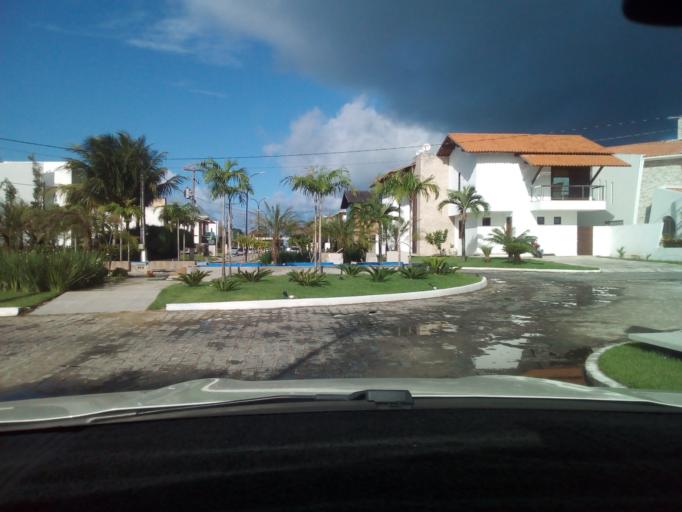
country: BR
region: Paraiba
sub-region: Joao Pessoa
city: Joao Pessoa
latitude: -7.1405
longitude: -34.8215
